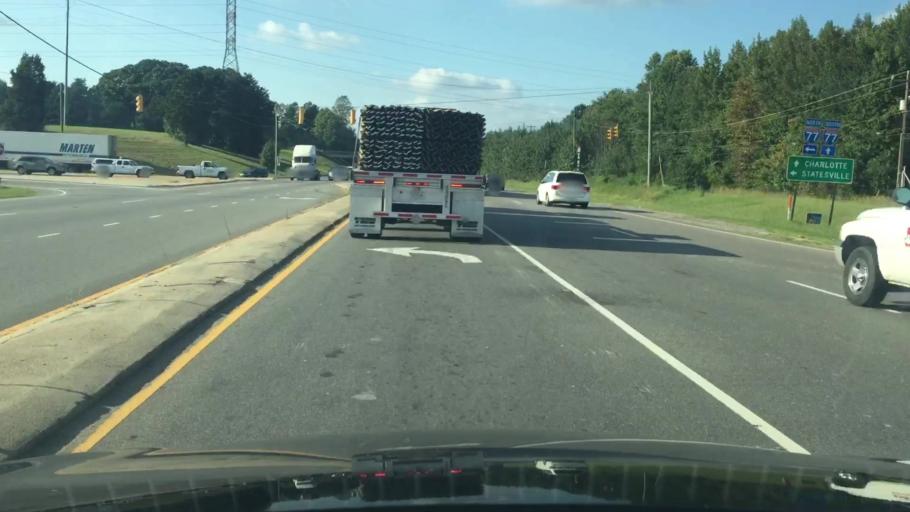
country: US
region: North Carolina
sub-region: Iredell County
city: Troutman
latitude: 35.6717
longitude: -80.8548
